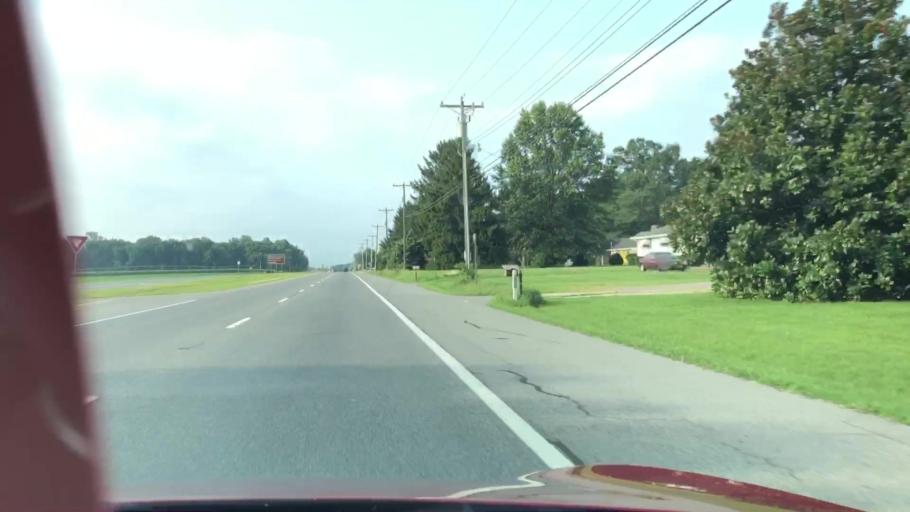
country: US
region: Delaware
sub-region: Kent County
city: Felton
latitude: 39.0185
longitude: -75.5657
